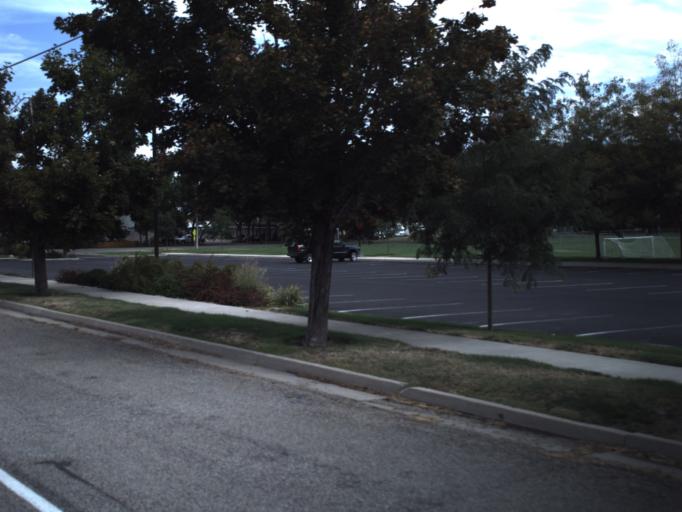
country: US
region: Utah
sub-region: Cache County
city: Mendon
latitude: 41.7089
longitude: -111.9792
